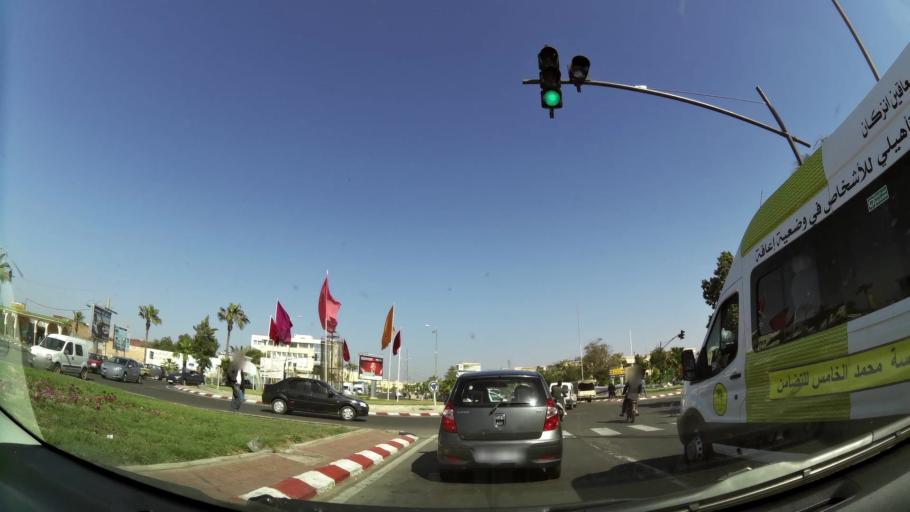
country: MA
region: Souss-Massa-Draa
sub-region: Inezgane-Ait Mellou
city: Inezgane
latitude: 30.3626
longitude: -9.5339
